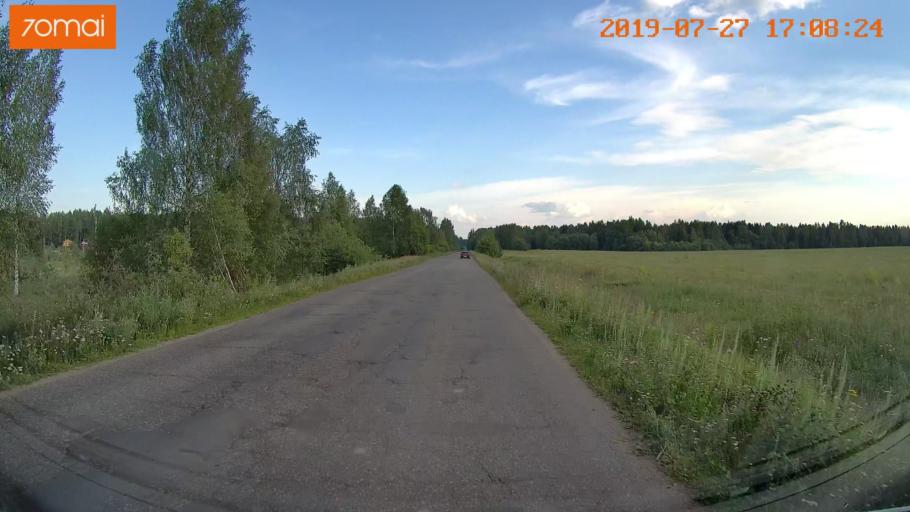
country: RU
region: Ivanovo
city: Novo-Talitsy
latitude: 57.0828
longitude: 40.8373
